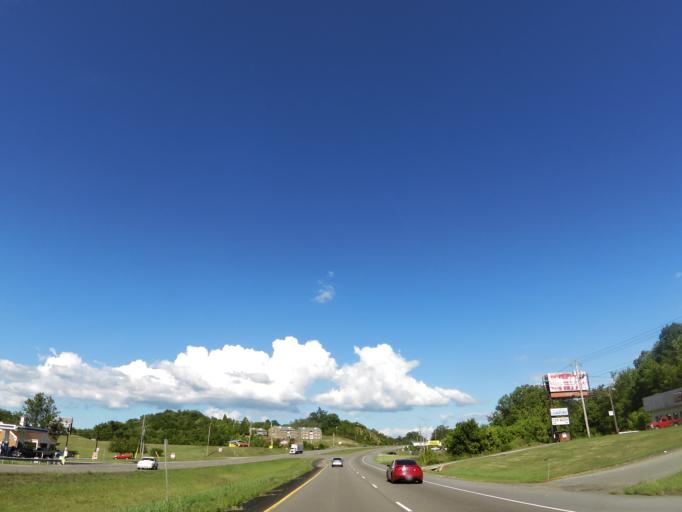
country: US
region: Tennessee
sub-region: Greene County
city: Mosheim
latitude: 36.1879
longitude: -82.9598
